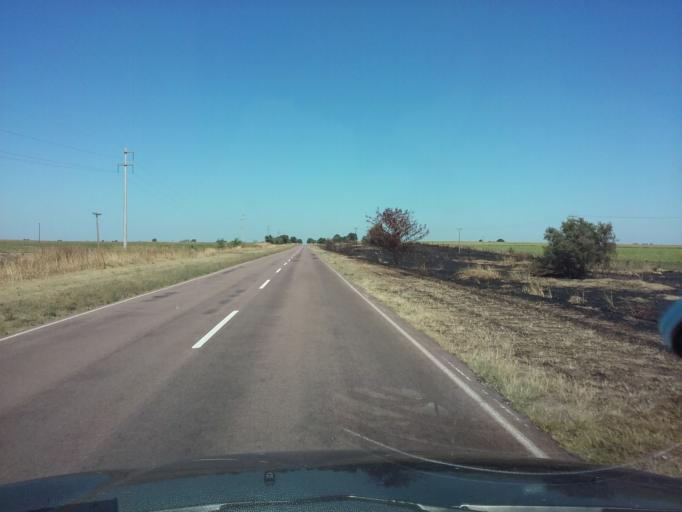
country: AR
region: La Pampa
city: Uriburu
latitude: -36.3881
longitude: -63.9432
